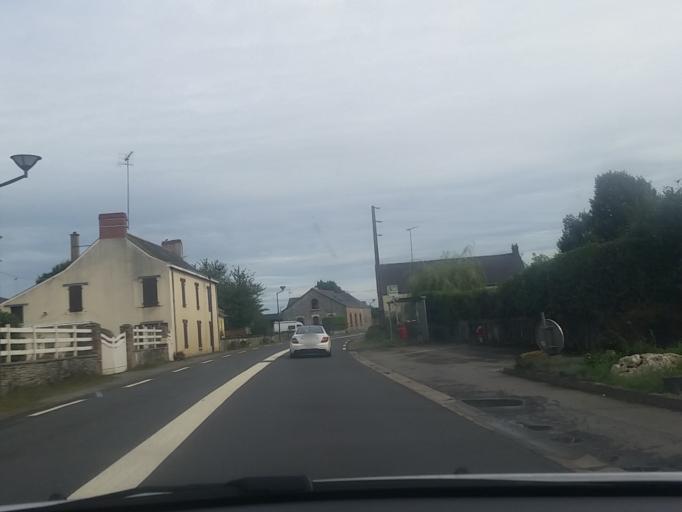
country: FR
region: Pays de la Loire
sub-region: Departement de la Loire-Atlantique
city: Saint-Vincent-des-Landes
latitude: 47.6208
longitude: -1.5370
